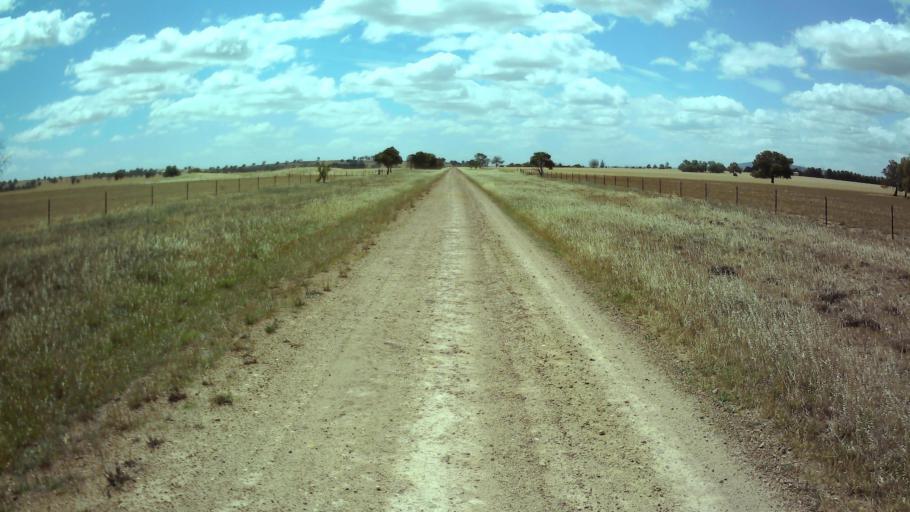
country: AU
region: New South Wales
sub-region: Weddin
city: Grenfell
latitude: -33.9890
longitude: 148.3177
